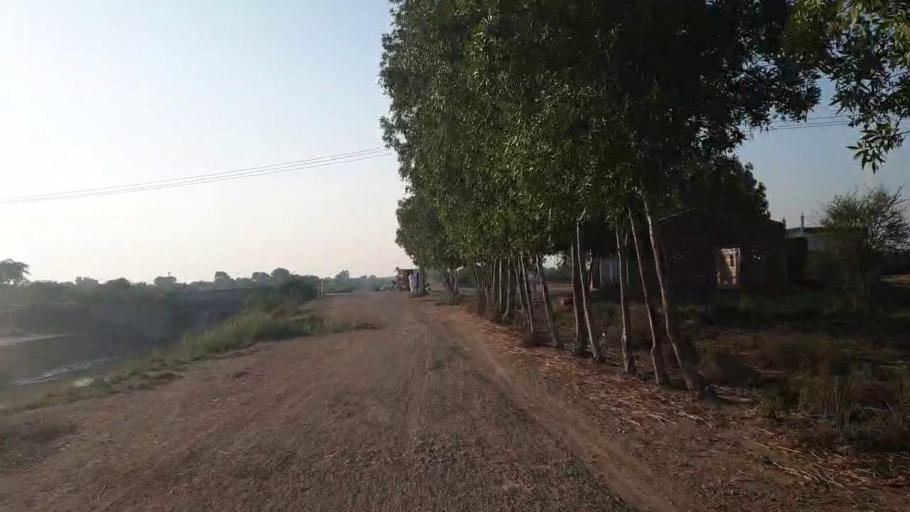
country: PK
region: Sindh
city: Badin
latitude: 24.6498
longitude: 68.7894
